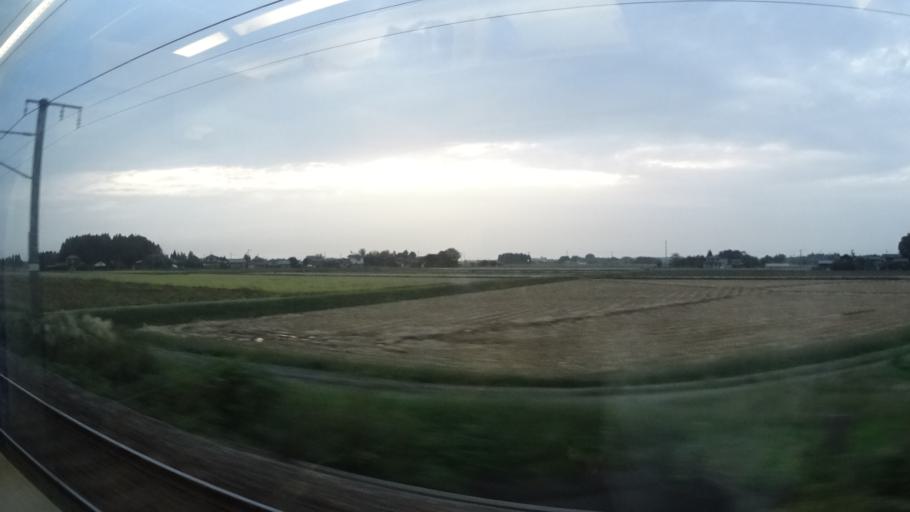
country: JP
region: Niigata
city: Murakami
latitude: 38.0892
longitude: 139.4244
